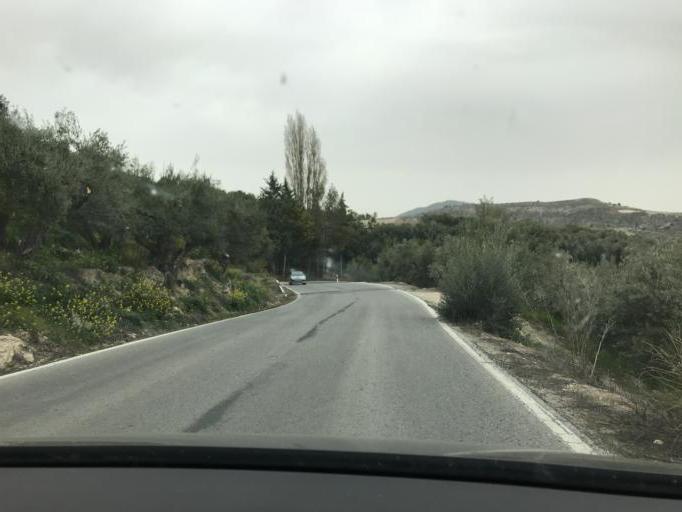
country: ES
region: Andalusia
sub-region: Provincia de Granada
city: Castril
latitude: 37.8012
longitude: -2.7722
